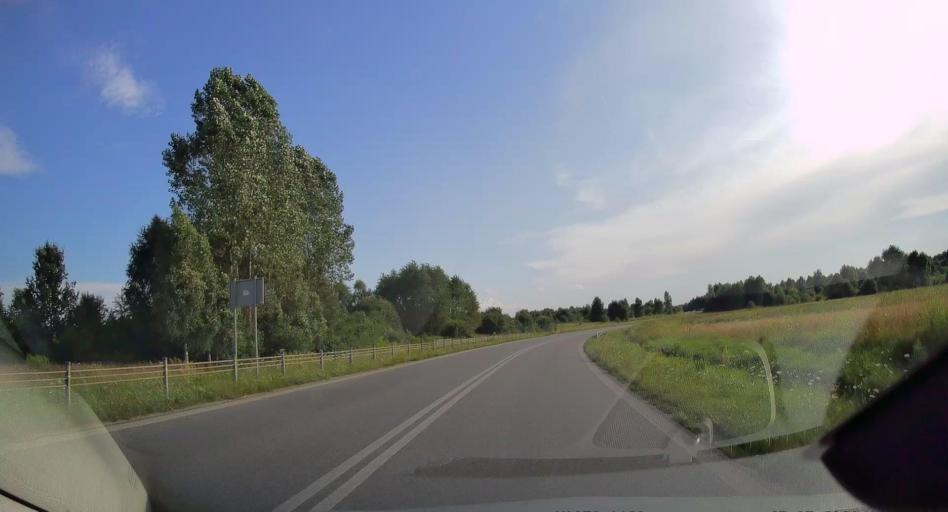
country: PL
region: Swietokrzyskie
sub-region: Powiat konecki
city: Konskie
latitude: 51.1831
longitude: 20.3948
